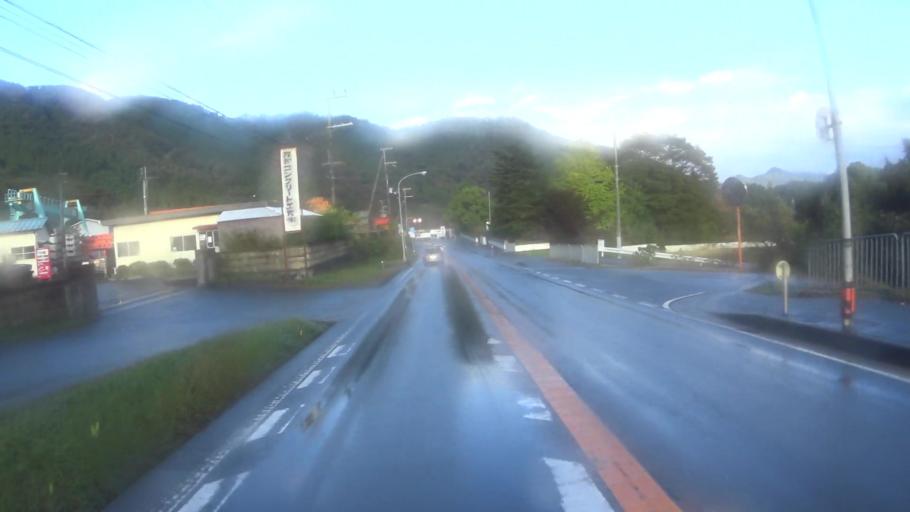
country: JP
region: Kyoto
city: Ayabe
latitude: 35.2312
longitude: 135.2235
